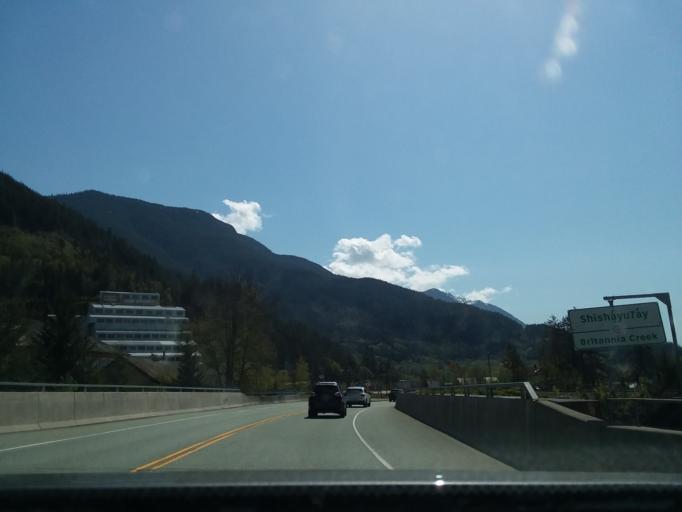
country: CA
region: British Columbia
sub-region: Greater Vancouver Regional District
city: Lions Bay
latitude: 49.6260
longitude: -123.2065
